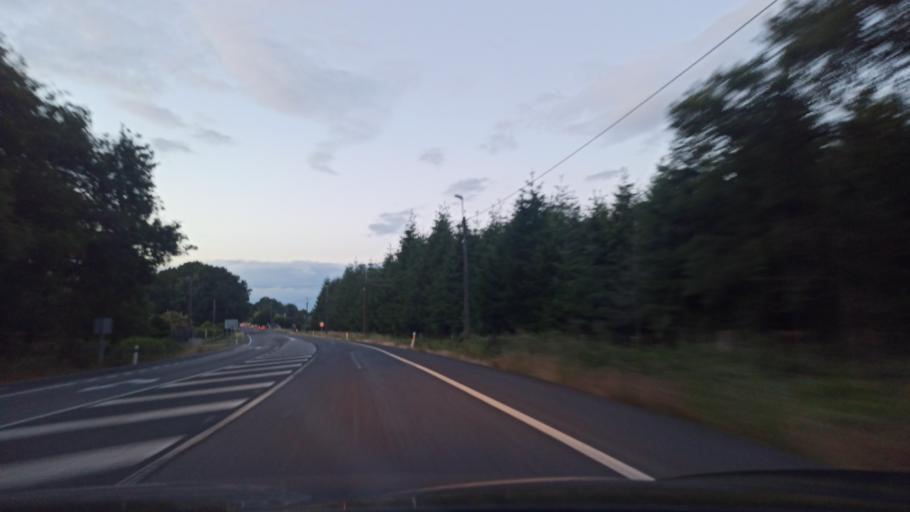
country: ES
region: Galicia
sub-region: Provincia de Lugo
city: Lugo
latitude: 42.9610
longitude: -7.6020
